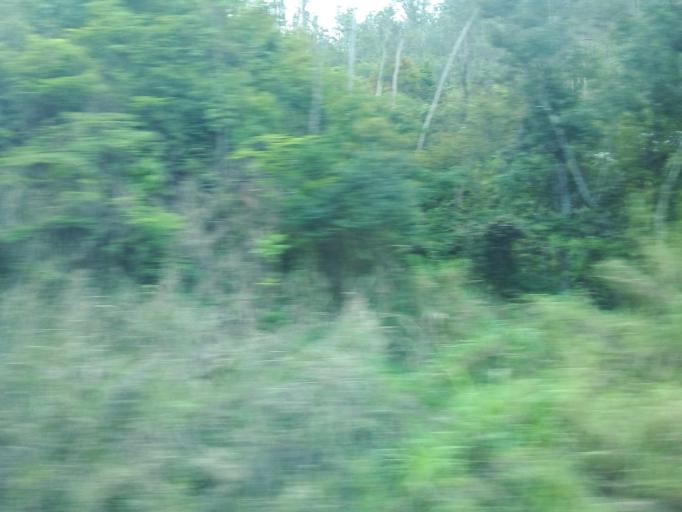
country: BR
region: Minas Gerais
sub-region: Joao Monlevade
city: Joao Monlevade
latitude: -19.8150
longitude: -43.1058
